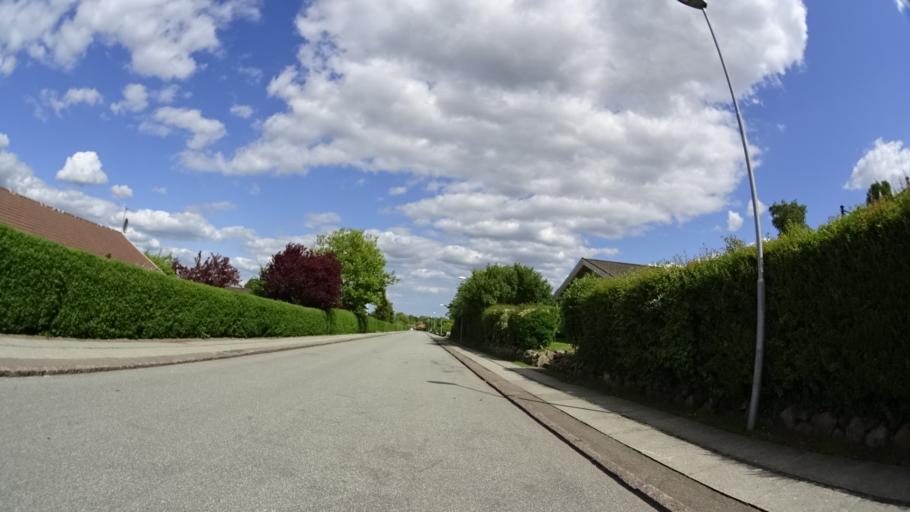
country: DK
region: Central Jutland
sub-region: Arhus Kommune
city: Stavtrup
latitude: 56.1317
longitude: 10.1174
